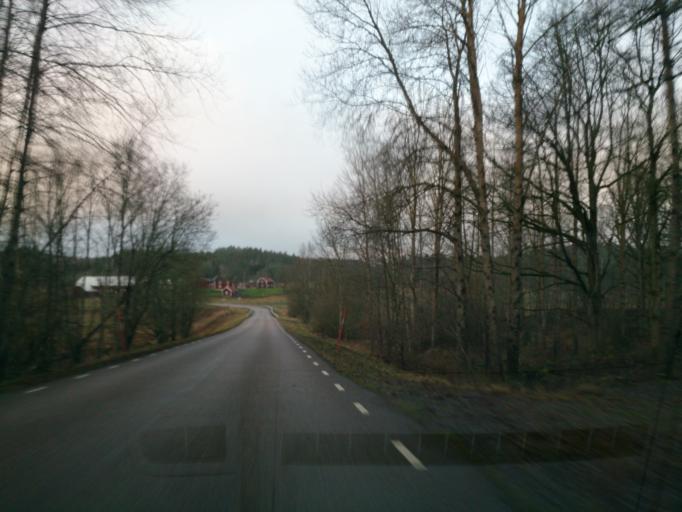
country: SE
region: OEstergoetland
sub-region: Atvidabergs Kommun
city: Atvidaberg
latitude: 58.2827
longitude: 16.0358
